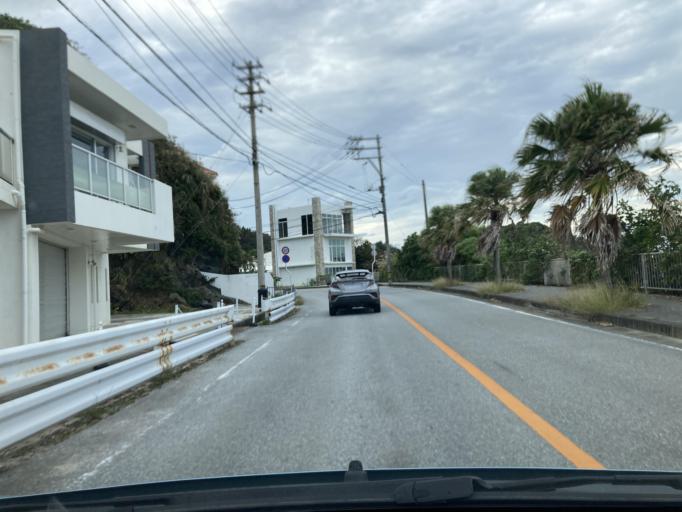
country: JP
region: Okinawa
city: Ishikawa
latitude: 26.4347
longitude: 127.7855
